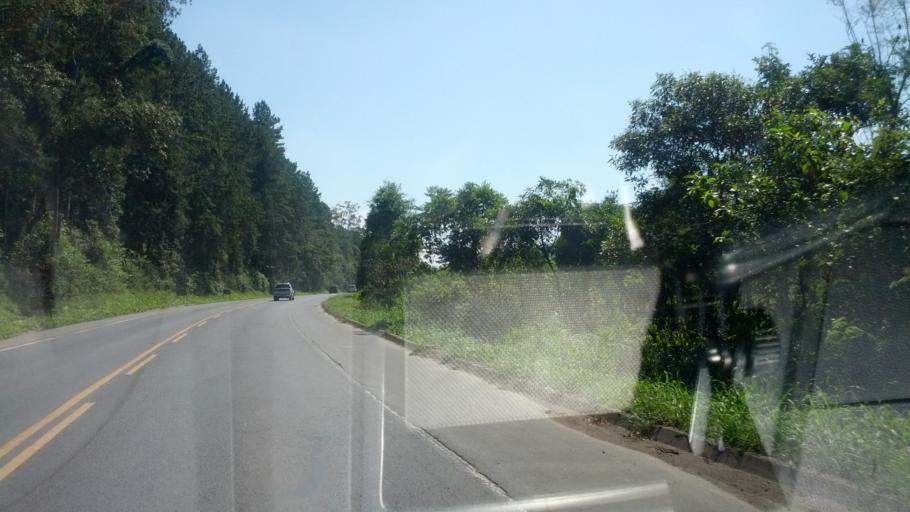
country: BR
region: Santa Catarina
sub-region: Rio Do Sul
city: Rio do Sul
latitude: -27.2370
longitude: -49.6819
